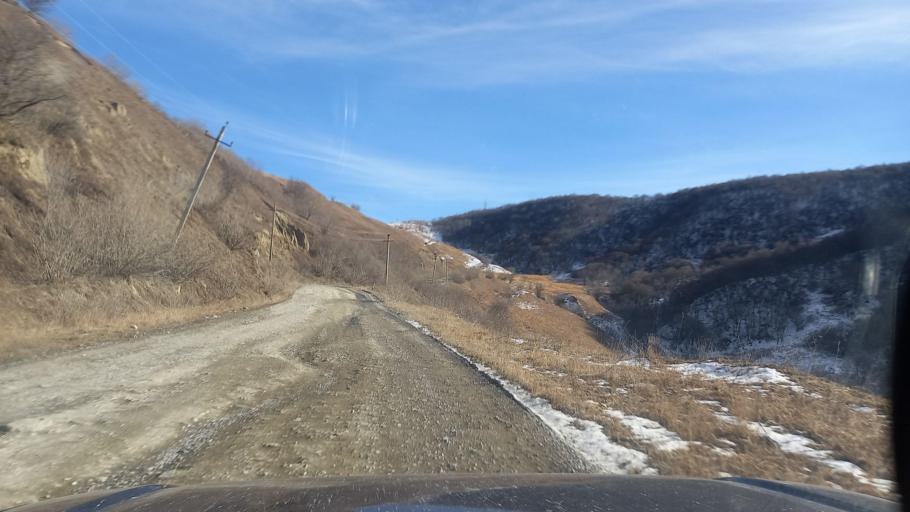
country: RU
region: North Ossetia
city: Verkhniy Fiagdon
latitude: 42.8364
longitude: 44.4686
